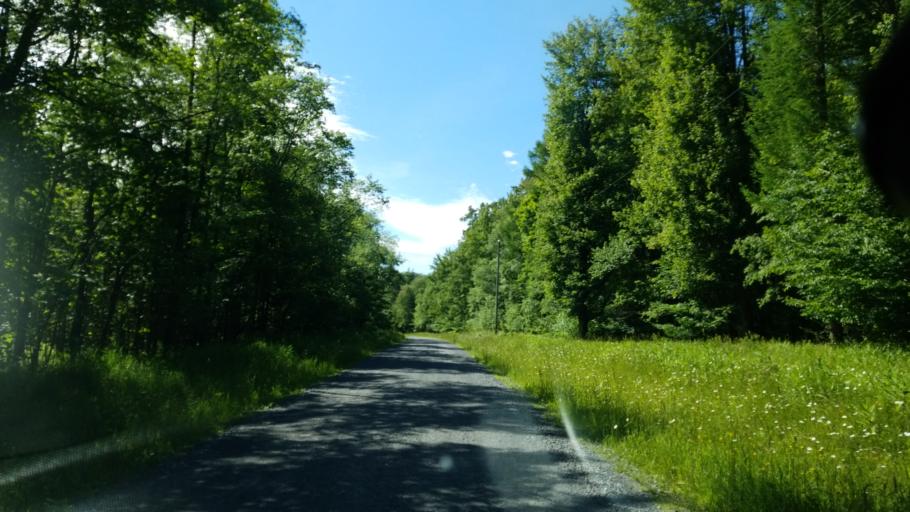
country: US
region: Pennsylvania
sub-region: Clearfield County
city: Clearfield
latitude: 41.1878
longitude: -78.4647
